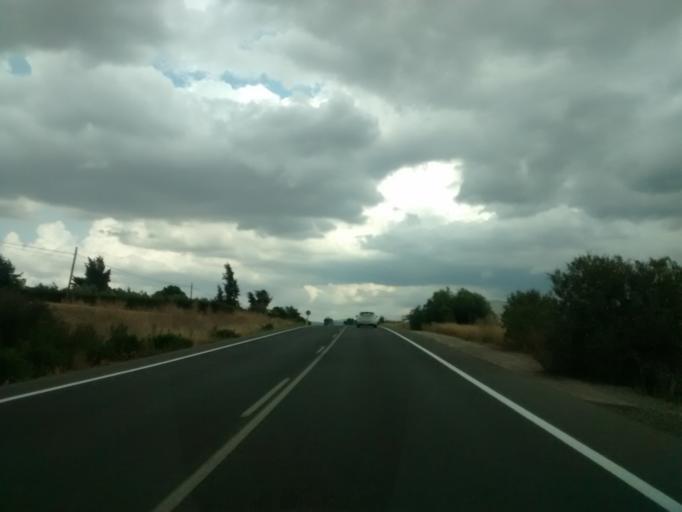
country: ES
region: Andalusia
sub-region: Provincia de Cadiz
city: Villamartin
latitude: 36.8610
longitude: -5.6182
